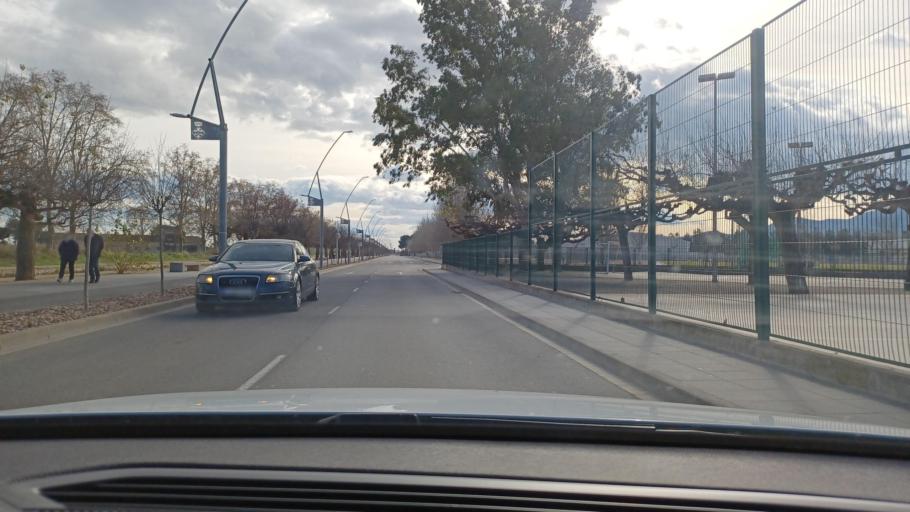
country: ES
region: Catalonia
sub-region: Provincia de Tarragona
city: Amposta
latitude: 40.7091
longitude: 0.5844
